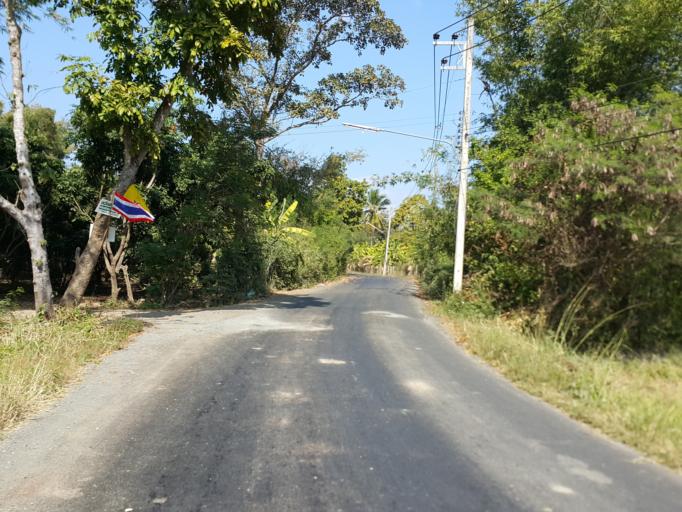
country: TH
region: Chiang Mai
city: Mae On
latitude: 18.8333
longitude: 99.2074
